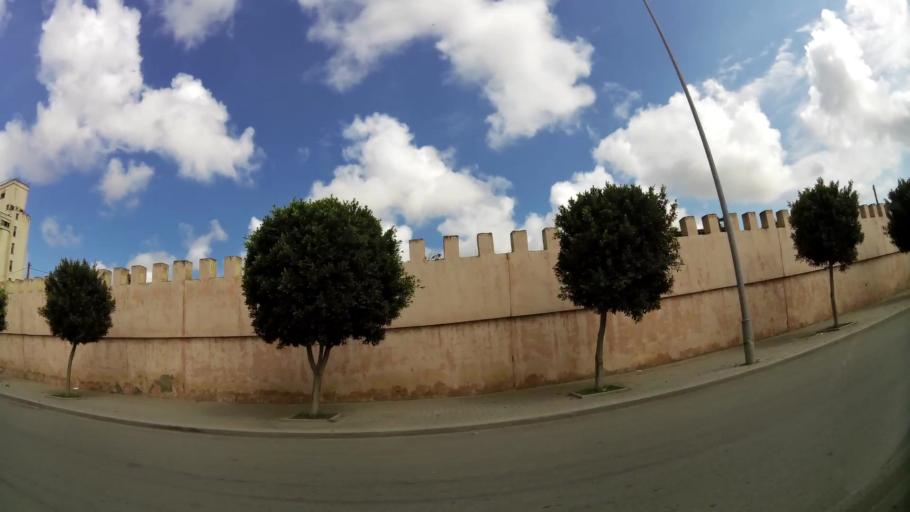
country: MA
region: Gharb-Chrarda-Beni Hssen
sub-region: Kenitra Province
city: Kenitra
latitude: 34.2661
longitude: -6.5770
